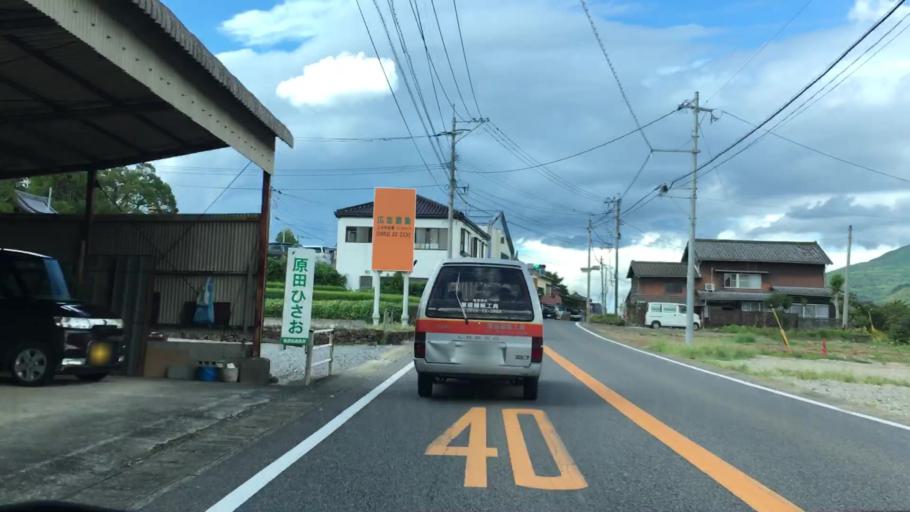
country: JP
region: Saga Prefecture
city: Imaricho-ko
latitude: 33.2043
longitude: 129.8501
